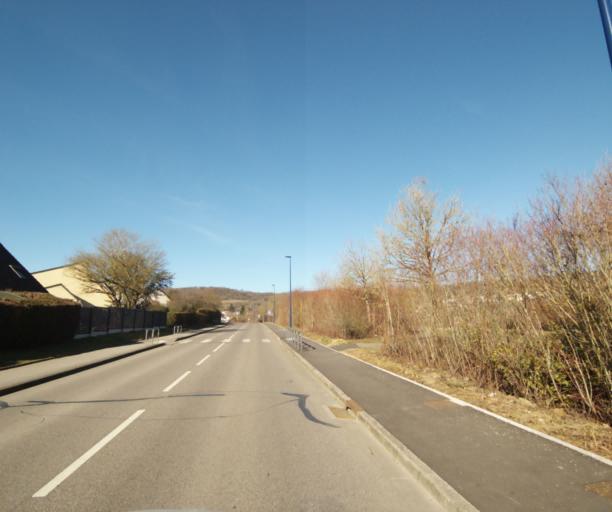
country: FR
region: Lorraine
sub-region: Departement de Meurthe-et-Moselle
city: Ludres
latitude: 48.6174
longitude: 6.1678
